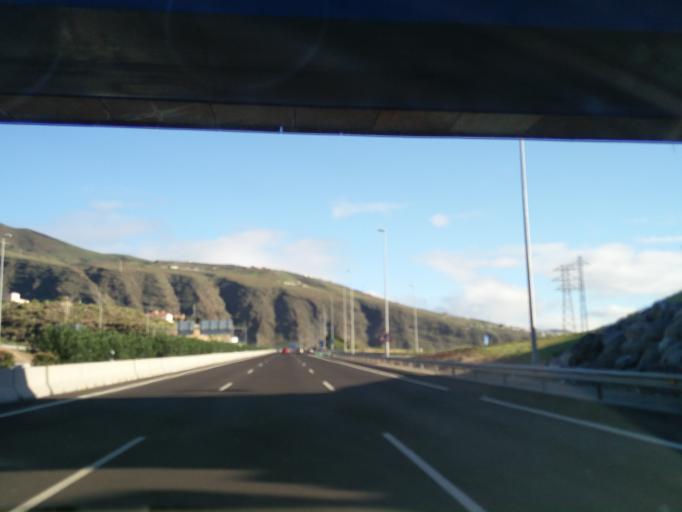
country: ES
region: Canary Islands
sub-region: Provincia de Santa Cruz de Tenerife
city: Candelaria
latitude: 28.3706
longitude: -16.3675
